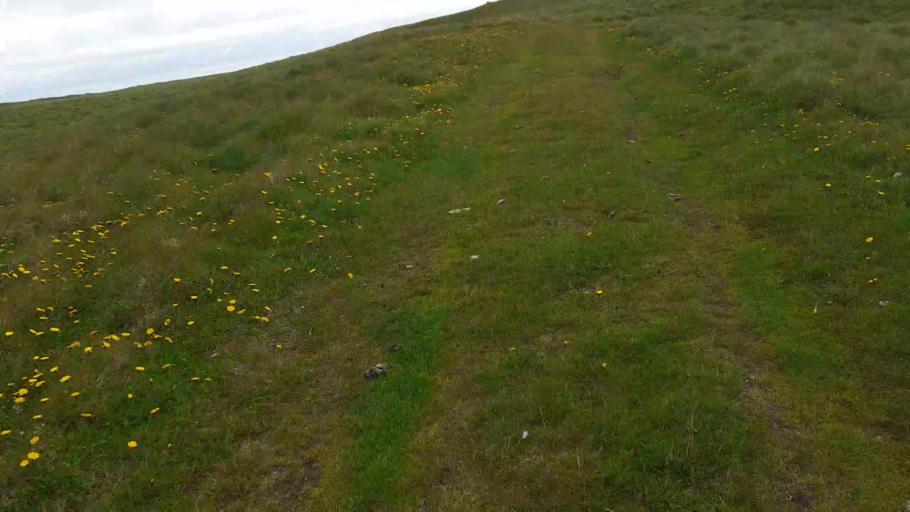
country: IS
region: Northeast
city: Dalvik
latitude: 66.5425
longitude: -17.9840
